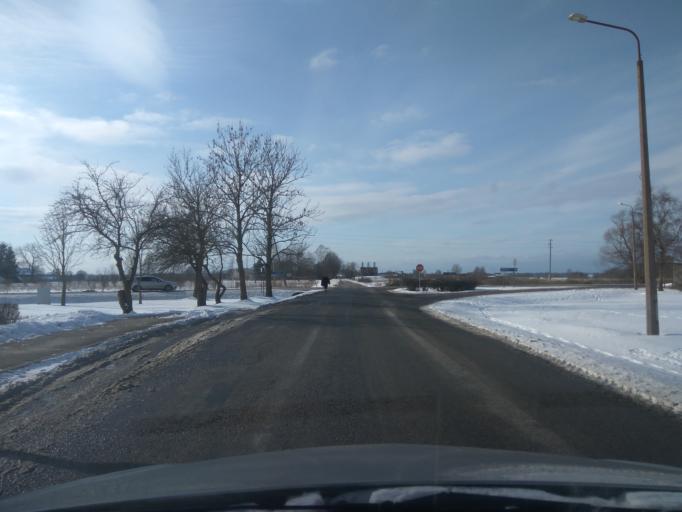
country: LV
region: Ventspils
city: Ventspils
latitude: 57.3327
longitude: 21.6359
